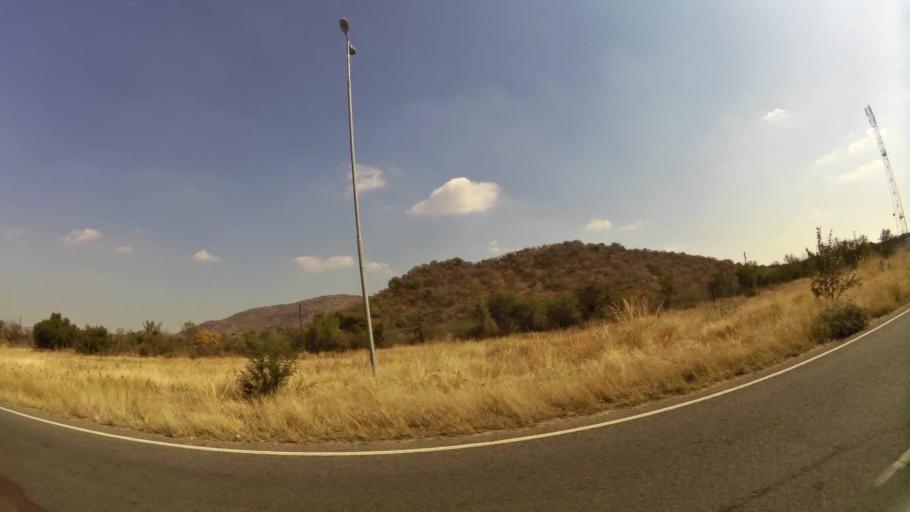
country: ZA
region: North-West
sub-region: Bojanala Platinum District Municipality
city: Rustenburg
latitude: -25.5395
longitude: 27.1224
